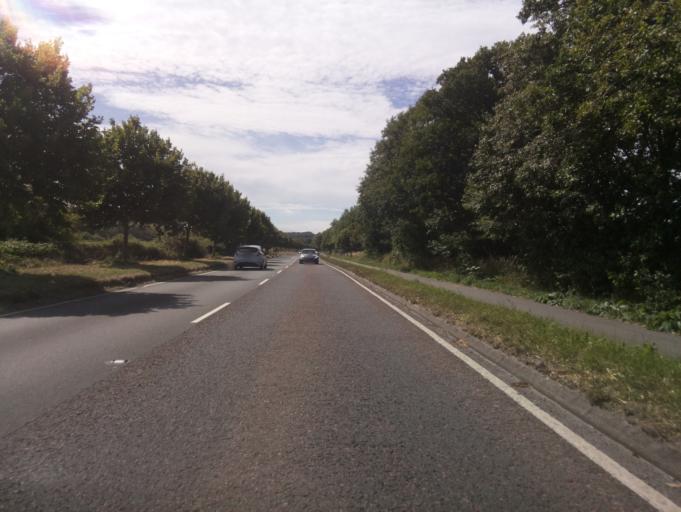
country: GB
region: England
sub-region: Dorset
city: Dorchester
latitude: 50.7210
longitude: -2.4461
